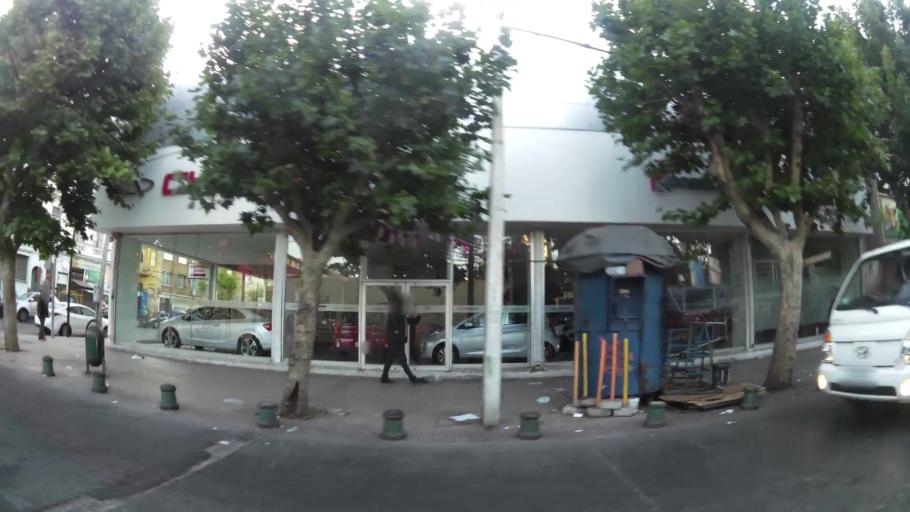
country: CL
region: Valparaiso
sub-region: Provincia de Valparaiso
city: Valparaiso
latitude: -33.0485
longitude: -71.6083
